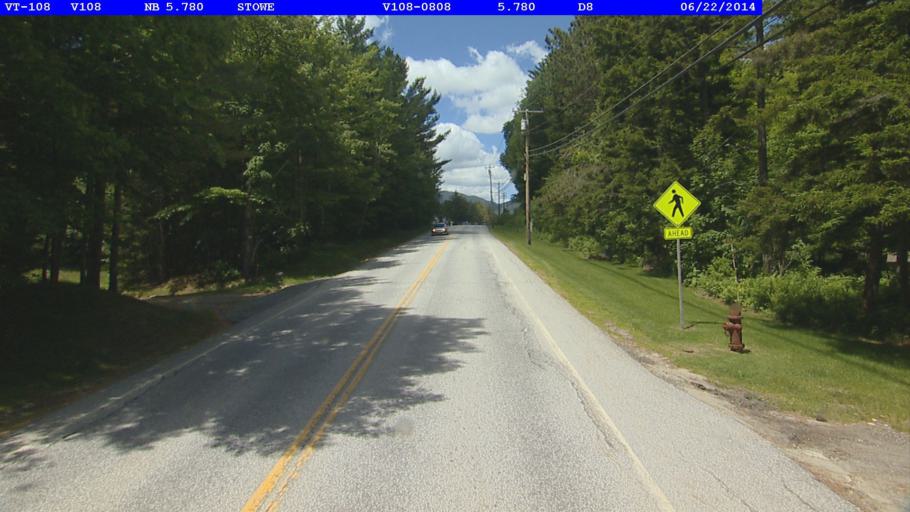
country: US
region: Vermont
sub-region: Lamoille County
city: Morristown
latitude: 44.5092
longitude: -72.7638
